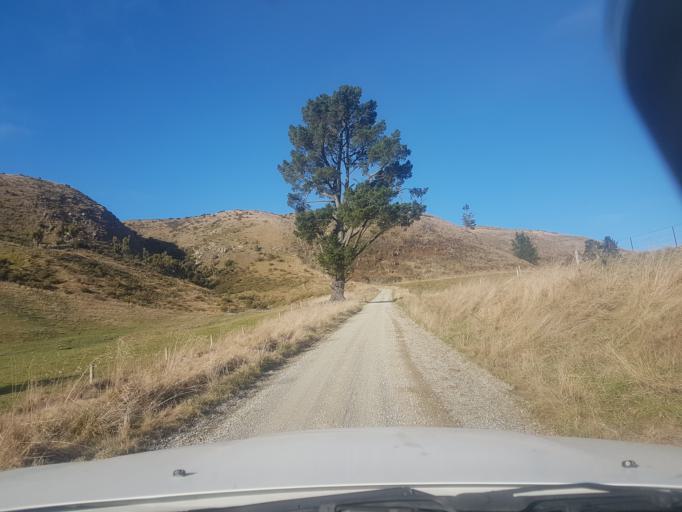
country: NZ
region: Canterbury
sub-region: Timaru District
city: Pleasant Point
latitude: -44.1654
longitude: 170.8782
